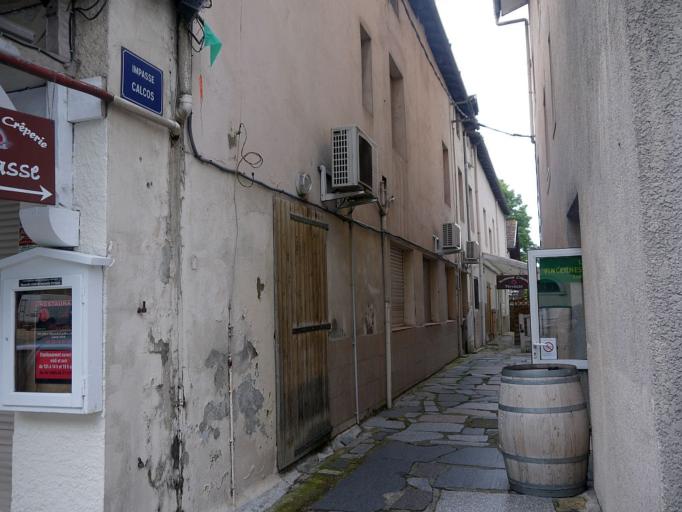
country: FR
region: Aquitaine
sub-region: Departement des Landes
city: Dax
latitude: 43.7134
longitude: -1.0558
